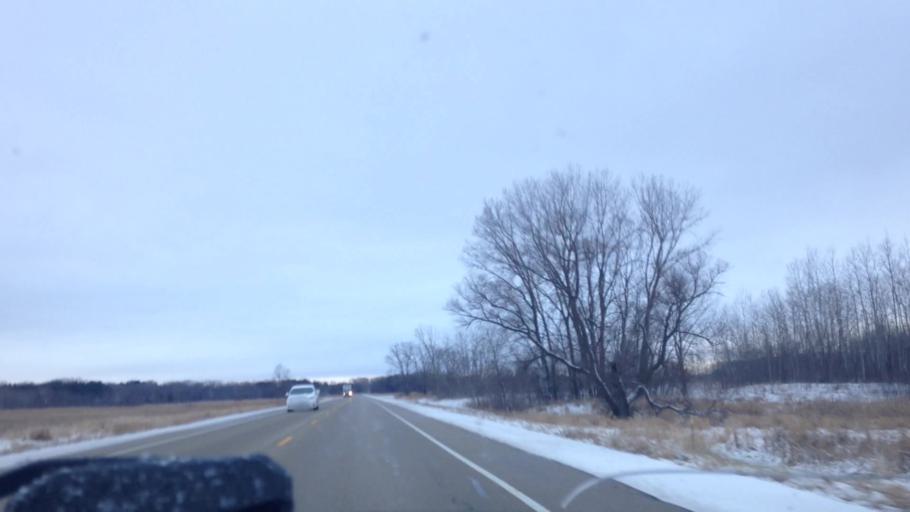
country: US
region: Wisconsin
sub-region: Dodge County
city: Horicon
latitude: 43.4688
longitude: -88.6061
